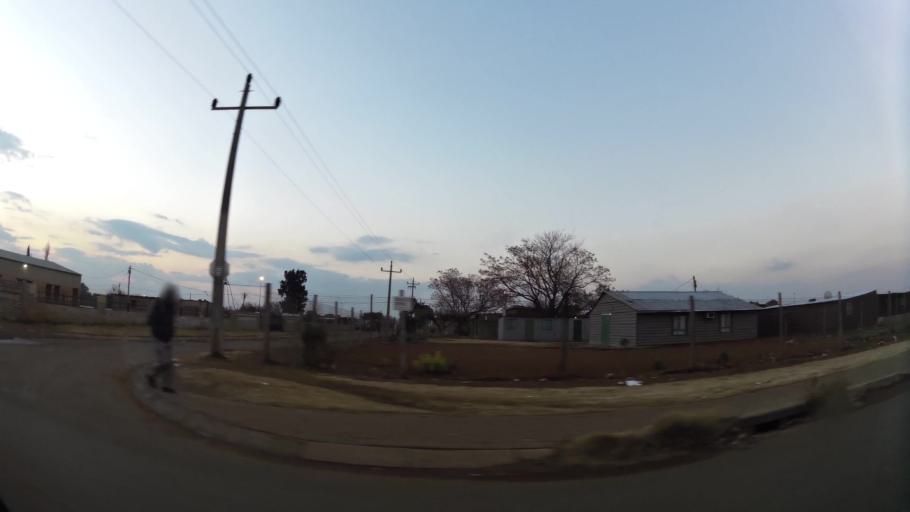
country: ZA
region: Gauteng
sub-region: City of Johannesburg Metropolitan Municipality
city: Orange Farm
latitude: -26.5539
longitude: 27.8494
